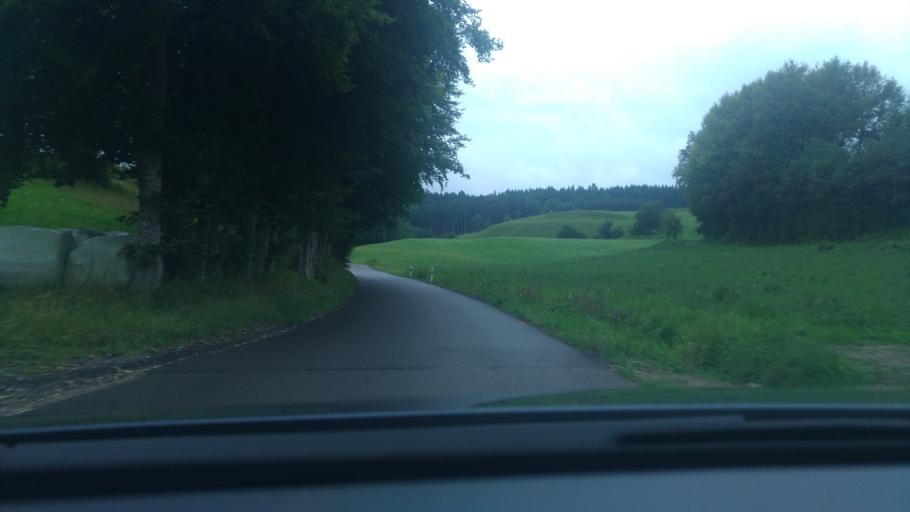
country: DE
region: Baden-Wuerttemberg
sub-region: Freiburg Region
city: Bodman-Ludwigshafen
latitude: 47.8553
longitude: 9.0980
